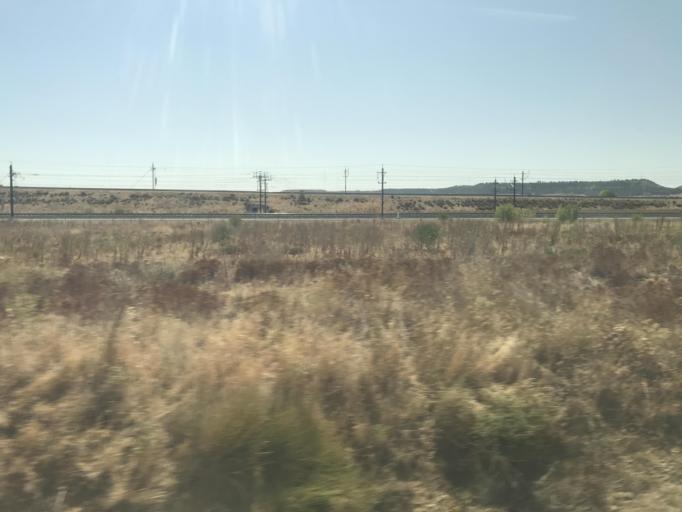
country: ES
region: Castille and Leon
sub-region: Provincia de Palencia
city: Venta de Banos
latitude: 41.9318
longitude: -4.4793
